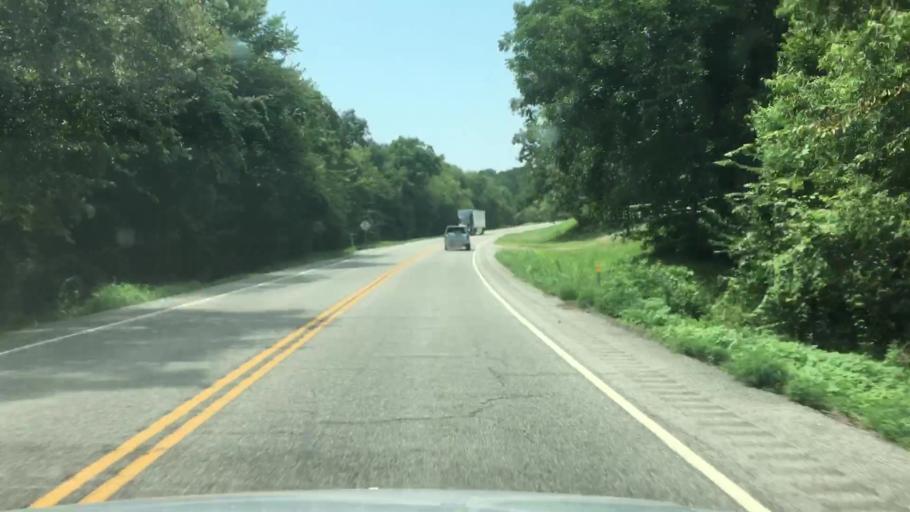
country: US
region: Oklahoma
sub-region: Muskogee County
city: Fort Gibson
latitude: 35.9307
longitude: -95.2339
